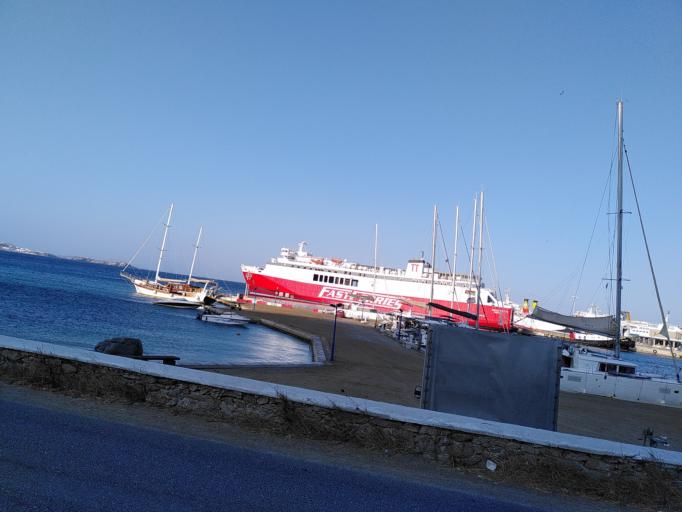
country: GR
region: South Aegean
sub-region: Nomos Kykladon
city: Mykonos
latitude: 37.4637
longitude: 25.3285
